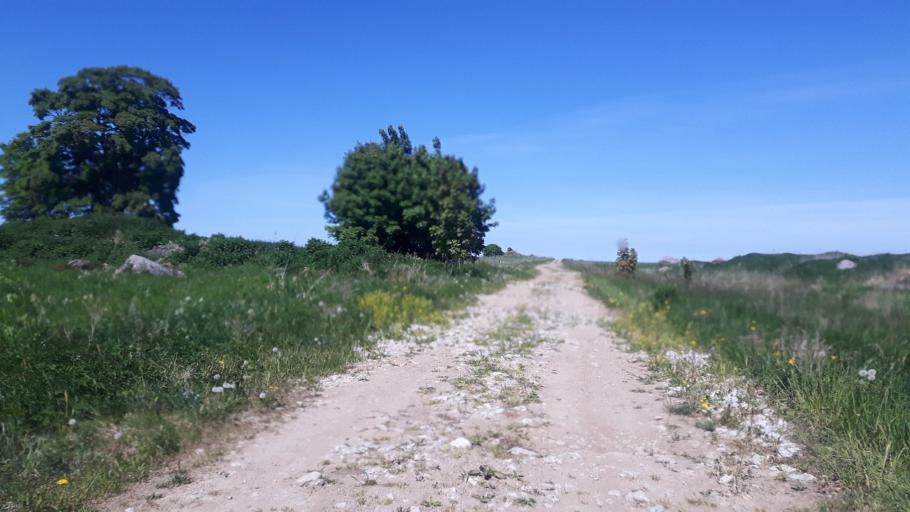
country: EE
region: Ida-Virumaa
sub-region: Toila vald
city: Voka
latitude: 59.4055
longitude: 27.6464
